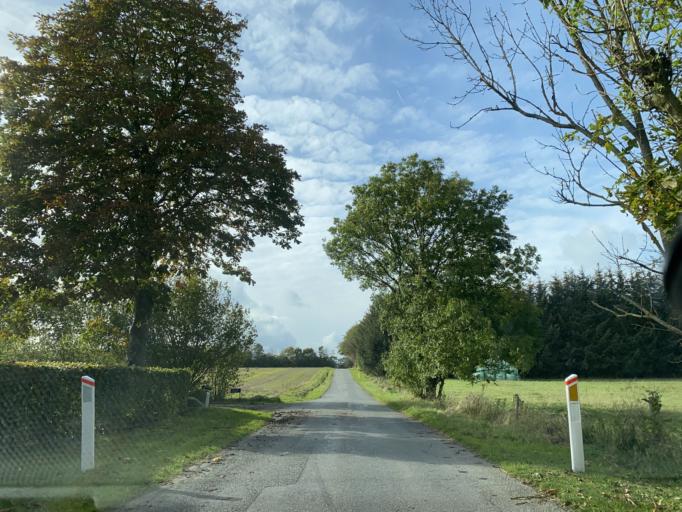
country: DK
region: Central Jutland
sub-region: Arhus Kommune
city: Sabro
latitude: 56.2110
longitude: 10.0024
